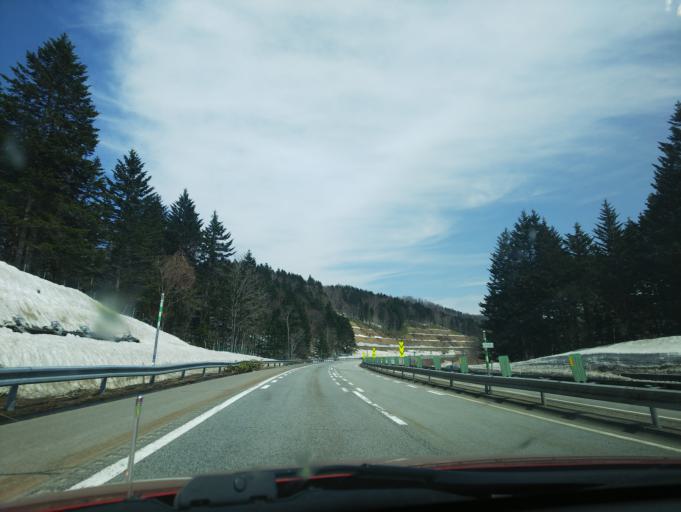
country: JP
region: Hokkaido
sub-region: Asahikawa-shi
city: Asahikawa
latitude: 43.7789
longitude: 142.1953
